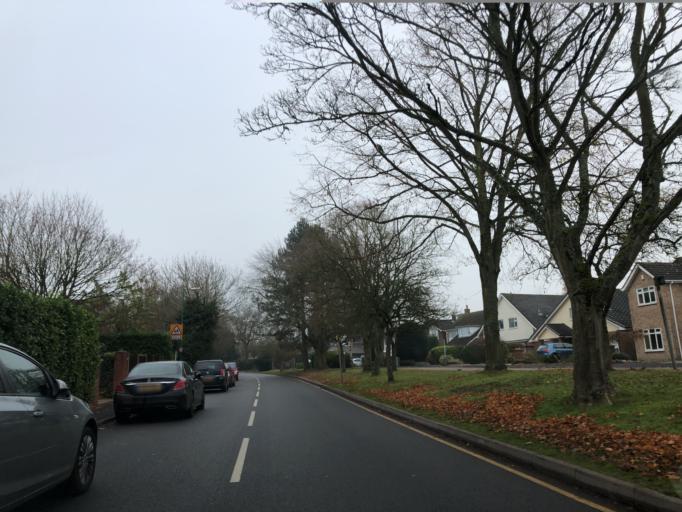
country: GB
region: England
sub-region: Solihull
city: Balsall Common
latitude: 52.3850
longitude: -1.6531
